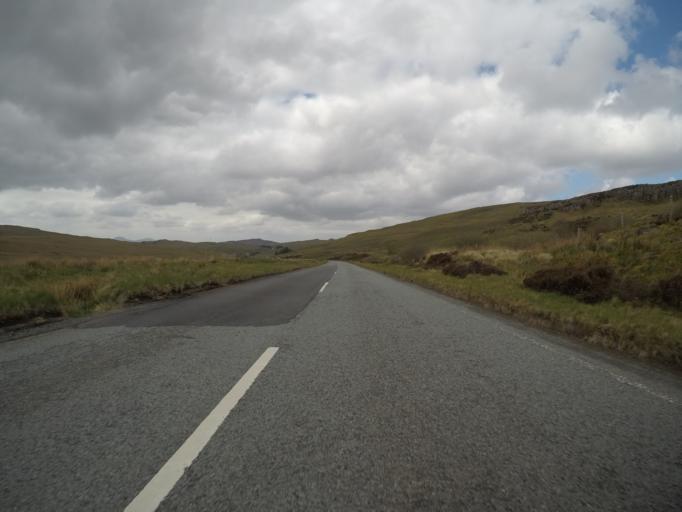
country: GB
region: Scotland
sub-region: Highland
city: Isle of Skye
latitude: 57.3180
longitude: -6.3221
